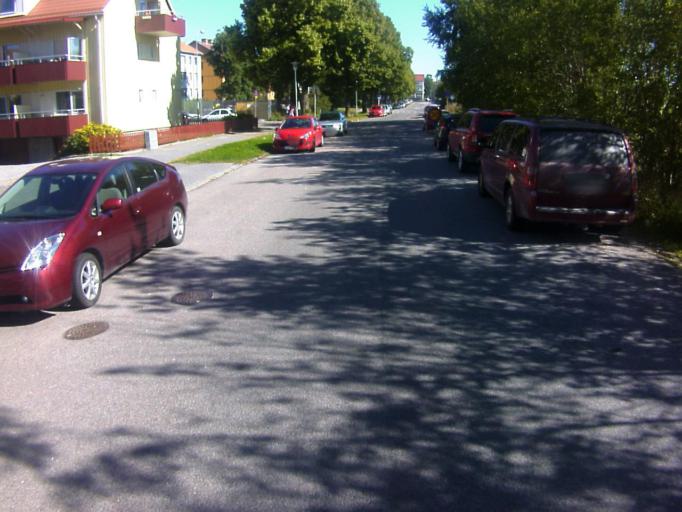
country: SE
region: Soedermanland
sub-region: Eskilstuna Kommun
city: Eskilstuna
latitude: 59.3799
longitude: 16.5165
